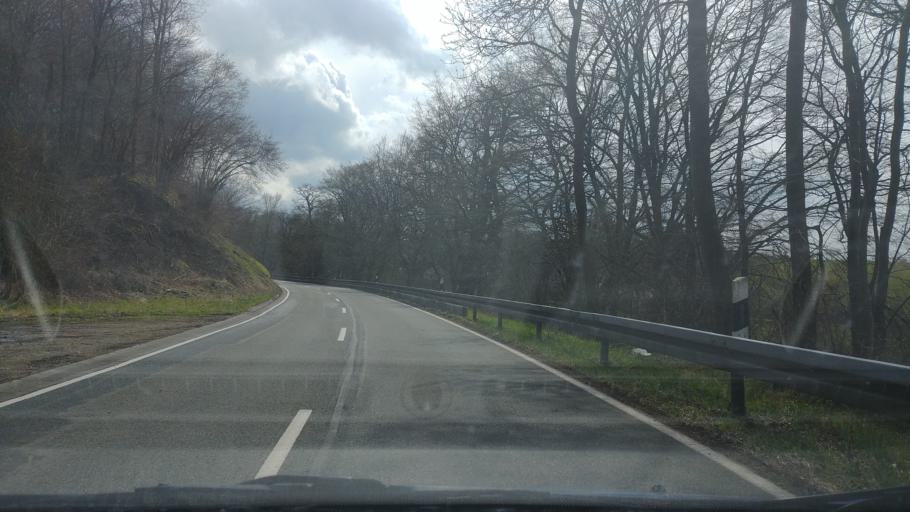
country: DE
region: Lower Saxony
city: Furstenberg
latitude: 51.7438
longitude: 9.4037
